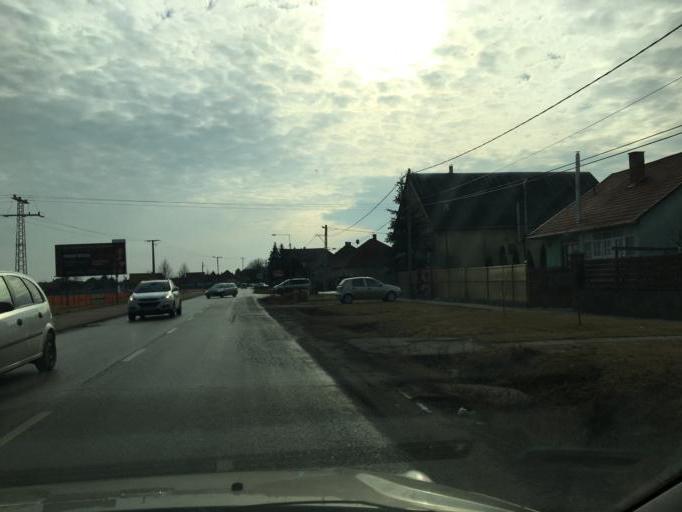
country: HU
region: Pest
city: Szigetszentmiklos
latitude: 47.3590
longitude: 19.0303
